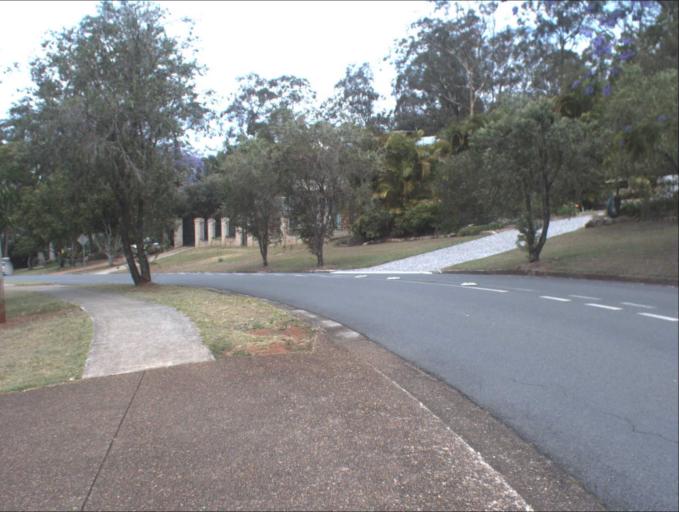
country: AU
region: Queensland
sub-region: Logan
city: Slacks Creek
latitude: -27.6723
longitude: 153.1747
